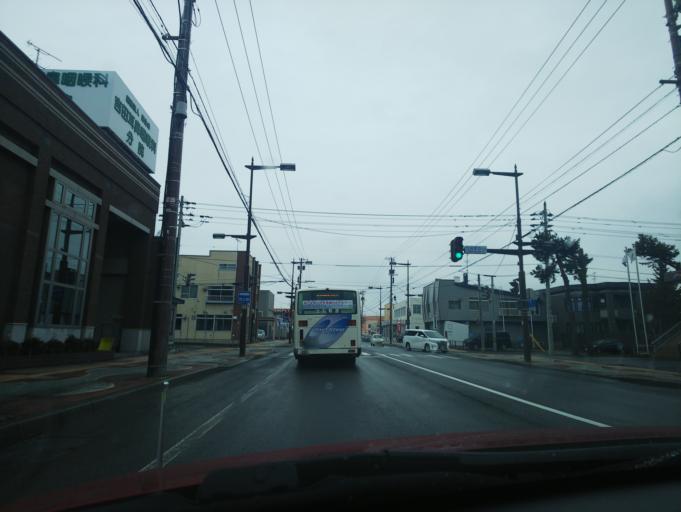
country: JP
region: Hokkaido
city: Nayoro
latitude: 44.1717
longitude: 142.3936
